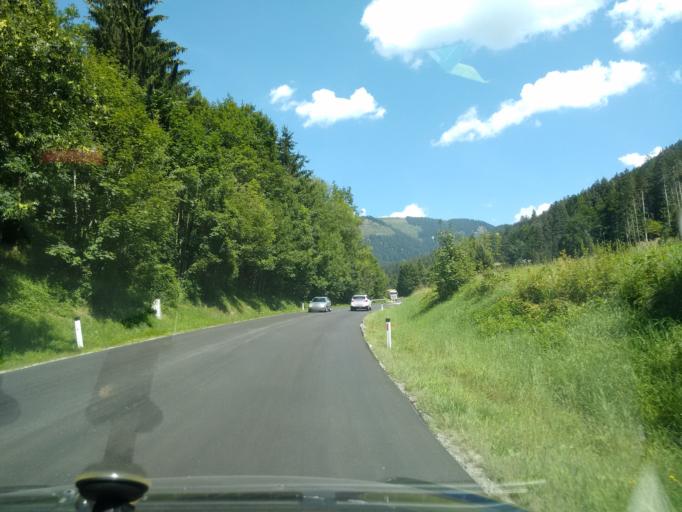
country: AT
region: Styria
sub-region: Politischer Bezirk Liezen
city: Liezen
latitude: 47.5796
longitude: 14.2643
